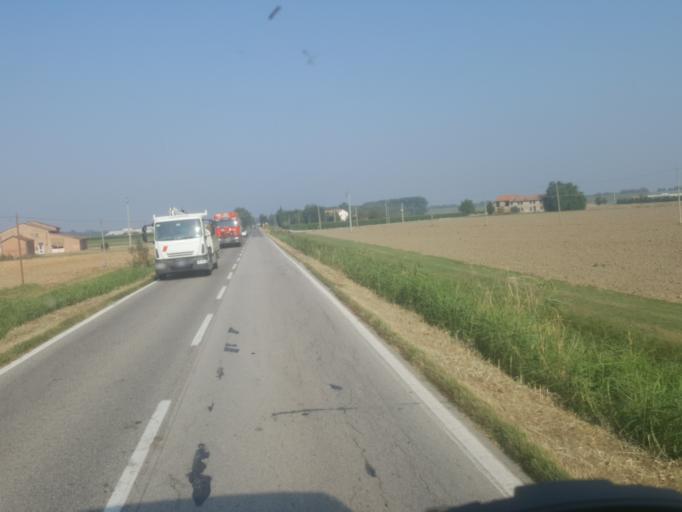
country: IT
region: Emilia-Romagna
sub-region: Provincia di Ravenna
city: Lavezzola
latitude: 44.5638
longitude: 11.9030
